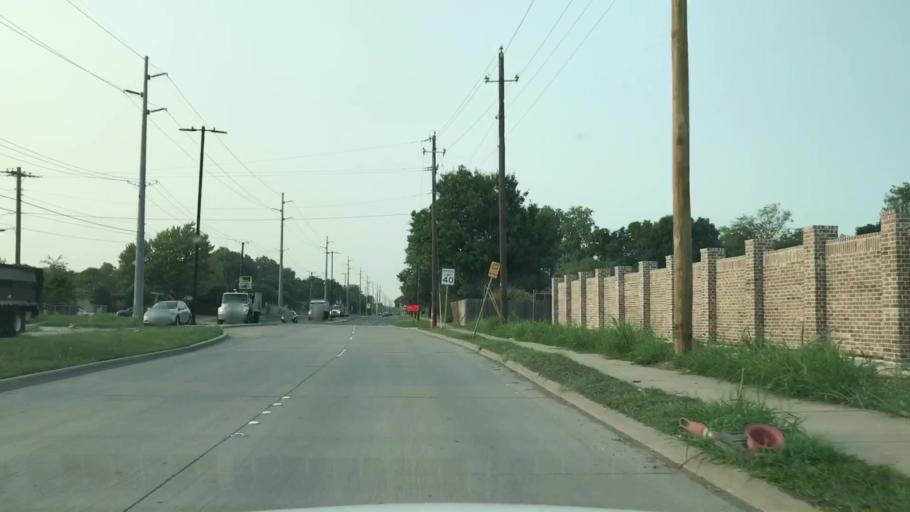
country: US
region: Texas
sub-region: Dallas County
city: Garland
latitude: 32.9149
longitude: -96.6136
